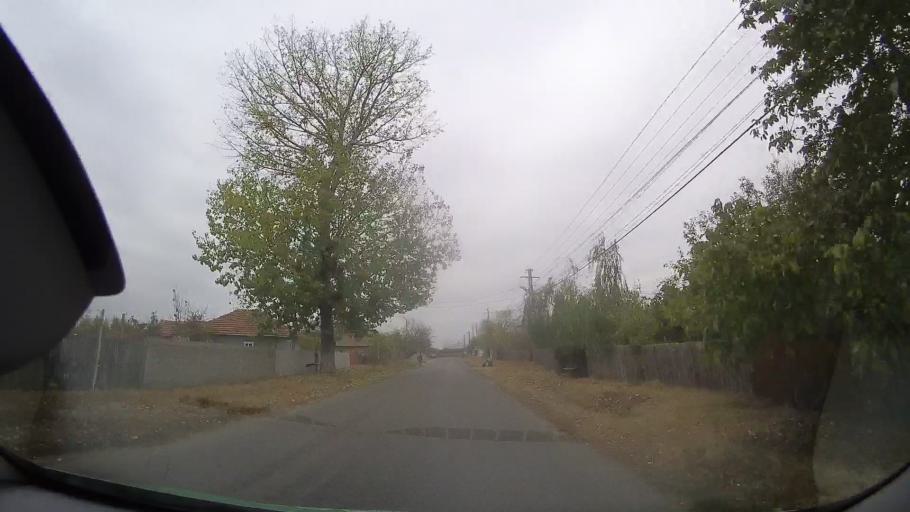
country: RO
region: Buzau
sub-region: Comuna Luciu
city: Luciu
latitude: 44.9813
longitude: 27.0378
